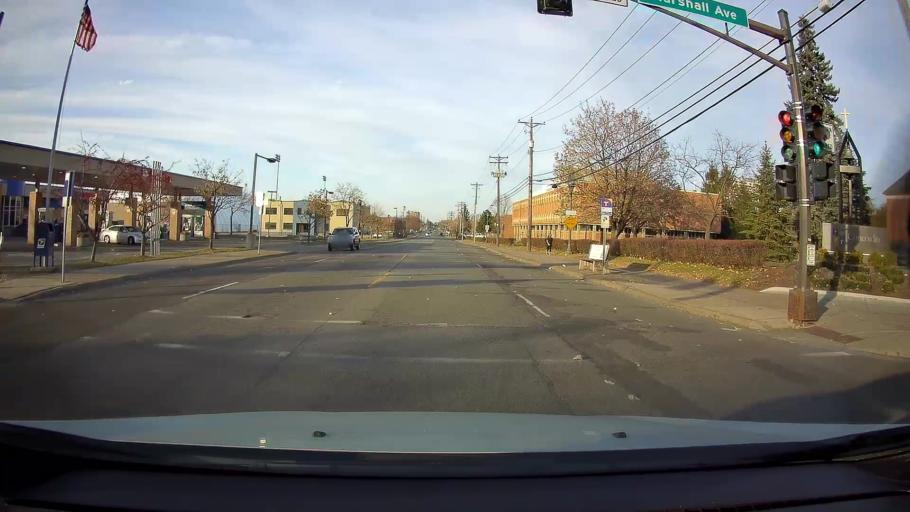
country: US
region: Minnesota
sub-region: Ramsey County
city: Falcon Heights
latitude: 44.9487
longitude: -93.1568
